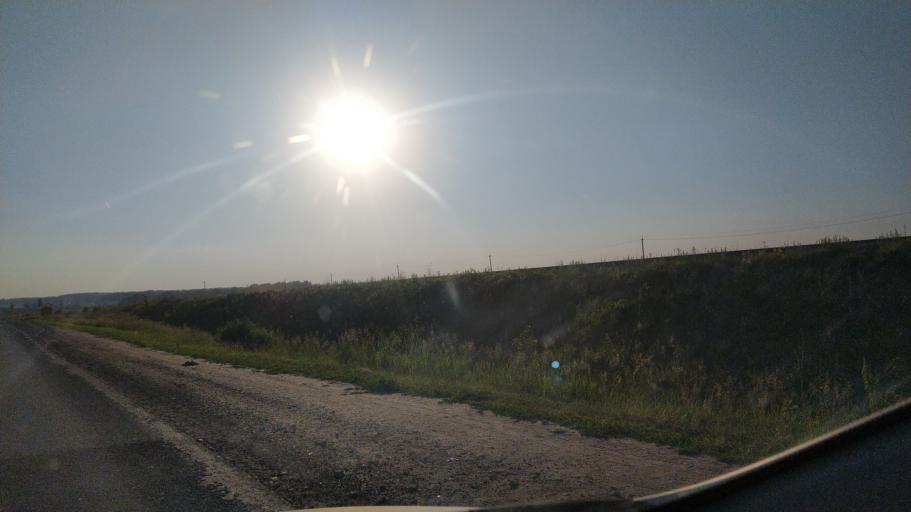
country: RU
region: Chuvashia
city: Kugesi
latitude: 56.0411
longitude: 47.3354
